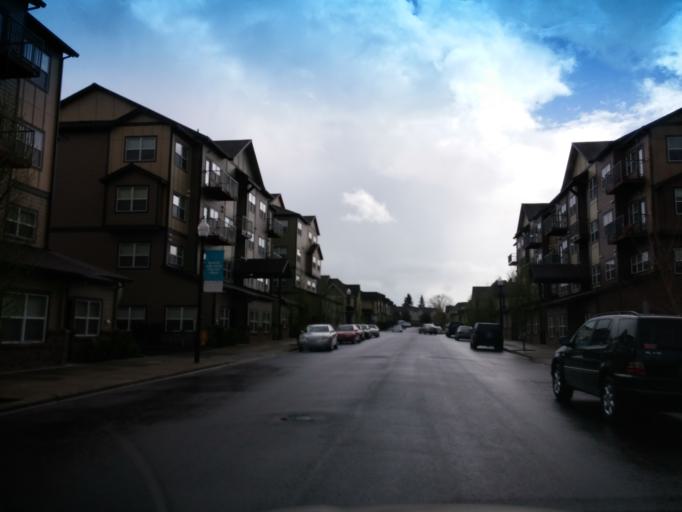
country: US
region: Oregon
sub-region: Washington County
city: Aloha
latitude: 45.5093
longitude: -122.8539
